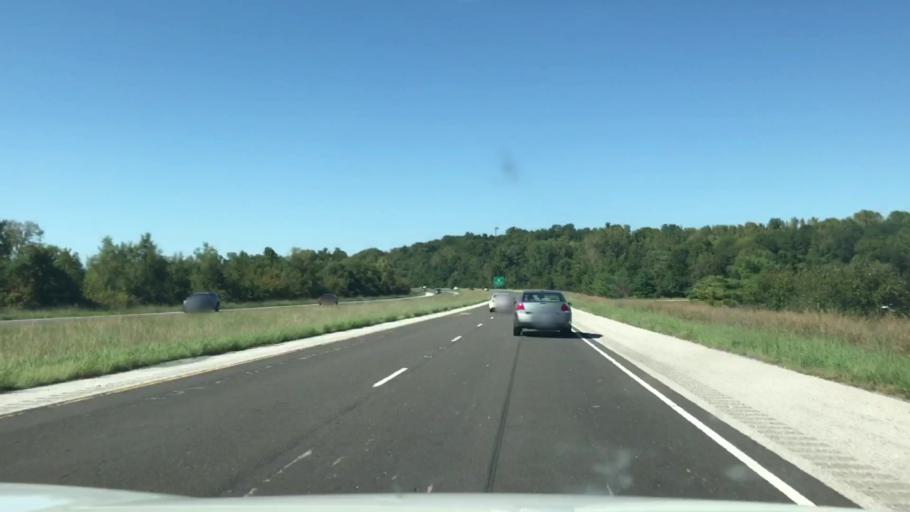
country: US
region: Illinois
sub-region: Madison County
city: South Roxana
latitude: 38.8362
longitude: -90.0435
